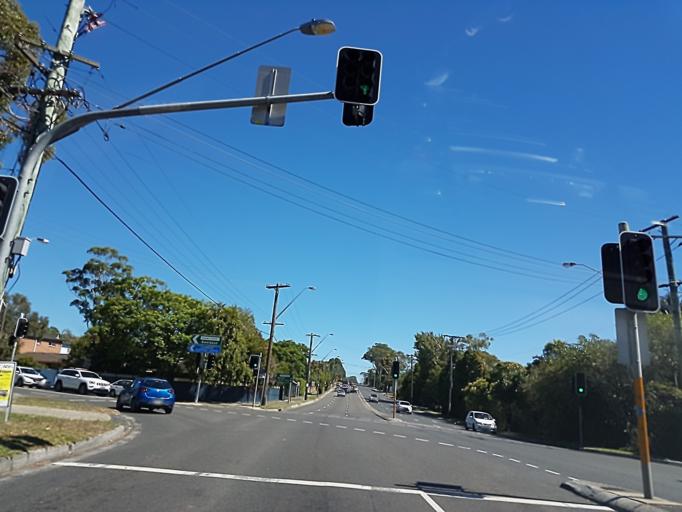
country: AU
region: New South Wales
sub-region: Warringah
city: Davidson
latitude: -33.7460
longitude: 151.2226
